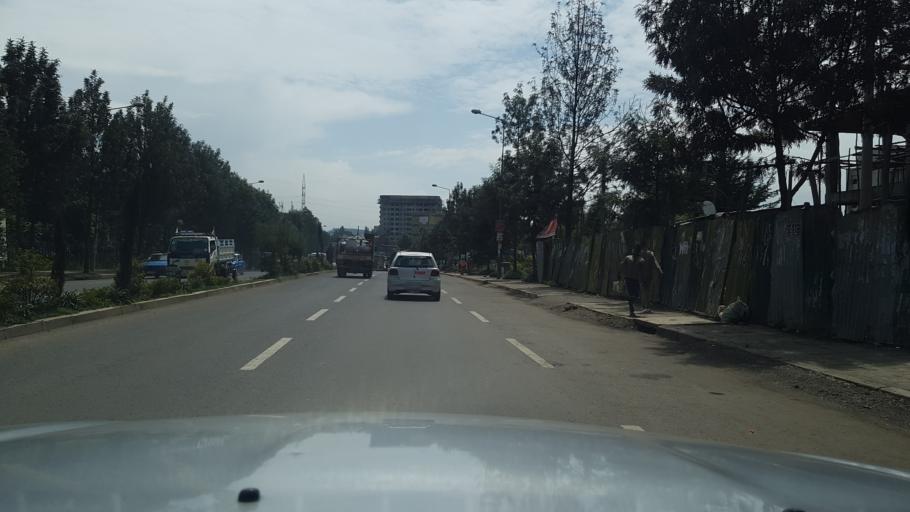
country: ET
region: Adis Abeba
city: Addis Ababa
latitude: 9.0252
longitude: 38.8244
